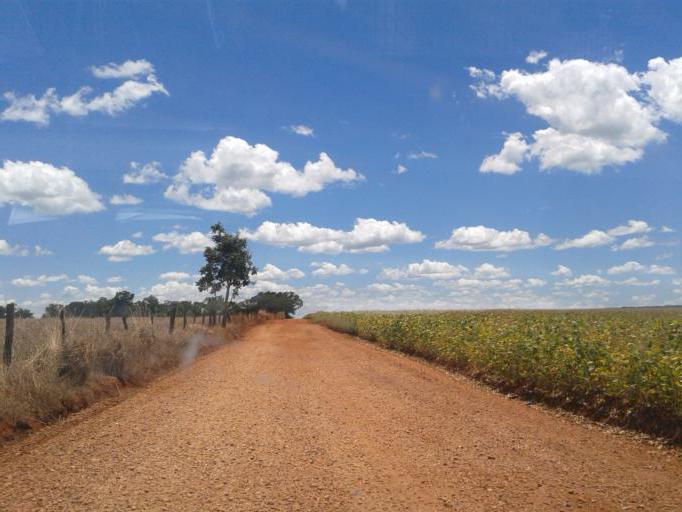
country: BR
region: Minas Gerais
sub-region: Capinopolis
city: Capinopolis
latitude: -18.5607
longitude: -49.5416
